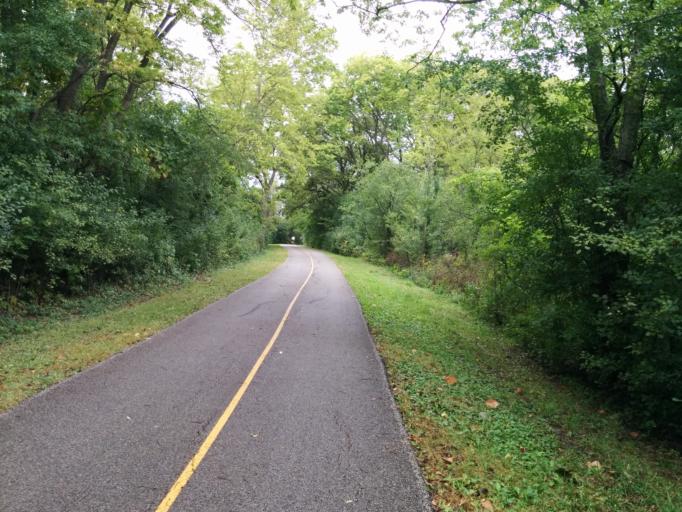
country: US
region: Illinois
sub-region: Cook County
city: Northfield
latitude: 42.1112
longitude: -87.7737
